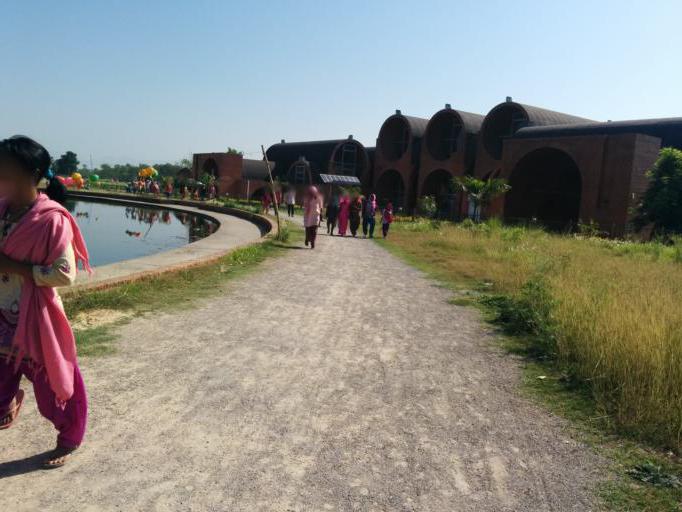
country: IN
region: Uttar Pradesh
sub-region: Maharajganj
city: Nautanwa
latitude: 27.4888
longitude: 83.2764
